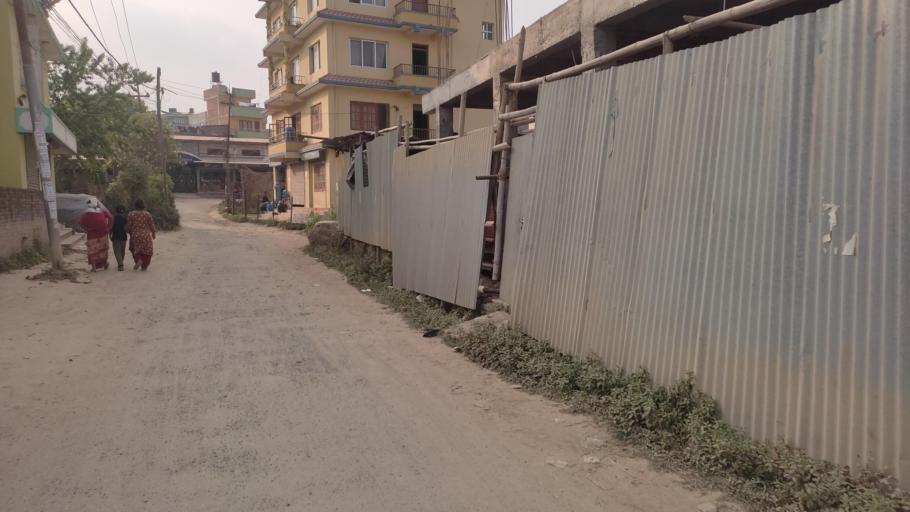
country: NP
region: Central Region
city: Kirtipur
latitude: 27.6714
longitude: 85.2773
